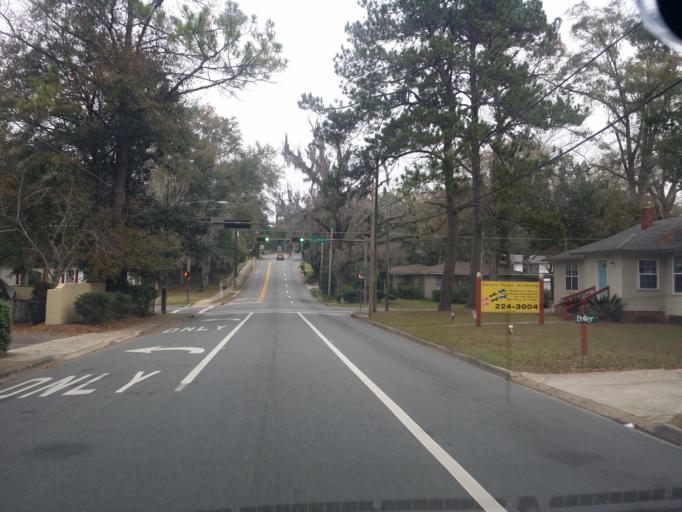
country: US
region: Florida
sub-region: Leon County
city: Tallahassee
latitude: 30.4532
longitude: -84.2831
